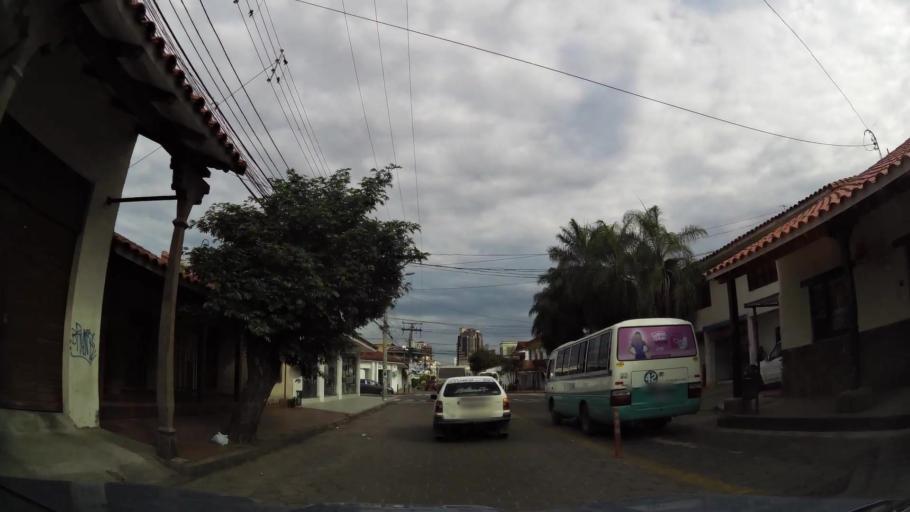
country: BO
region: Santa Cruz
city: Santa Cruz de la Sierra
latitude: -17.7860
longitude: -63.1779
